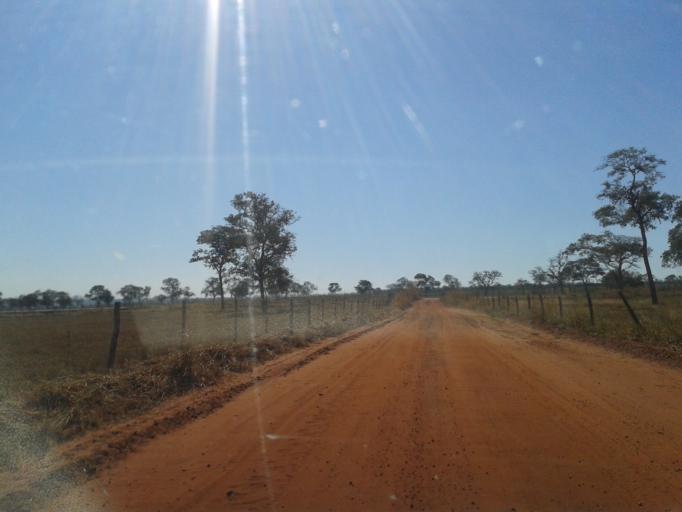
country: BR
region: Minas Gerais
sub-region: Santa Vitoria
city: Santa Vitoria
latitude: -19.0302
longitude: -50.3659
